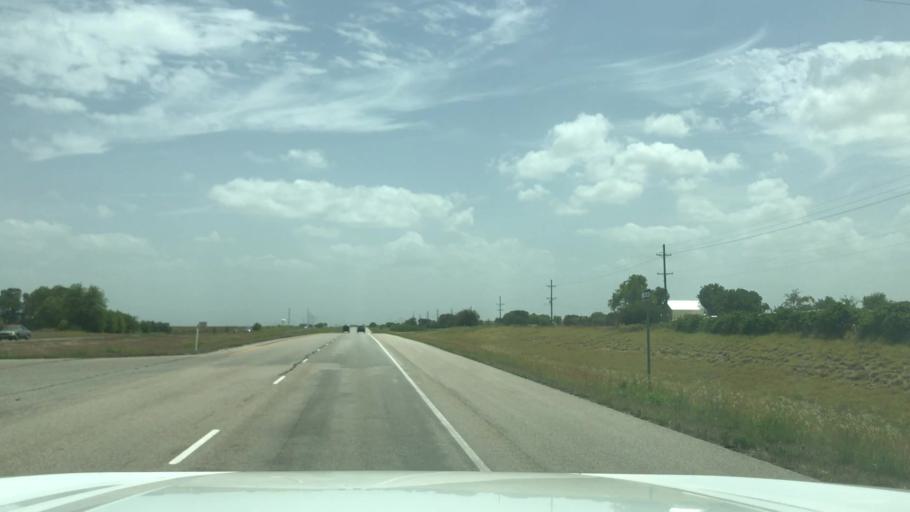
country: US
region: Texas
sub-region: Falls County
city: Marlin
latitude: 31.3469
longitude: -96.8948
